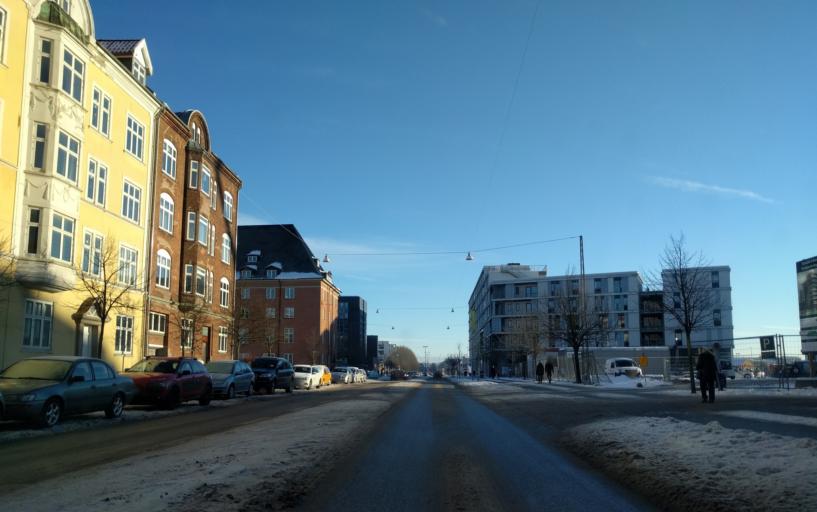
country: DK
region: North Denmark
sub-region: Alborg Kommune
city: Aalborg
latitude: 57.0425
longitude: 9.9215
